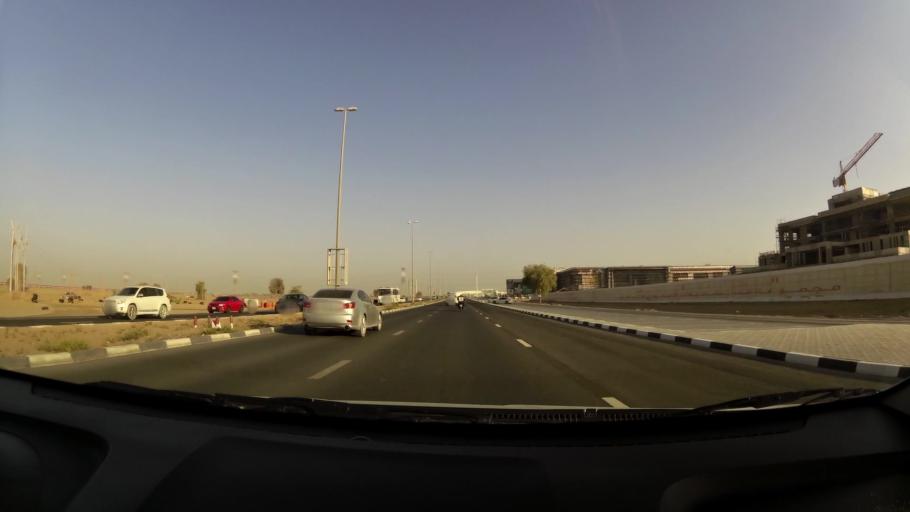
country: AE
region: Ajman
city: Ajman
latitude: 25.3687
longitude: 55.5108
